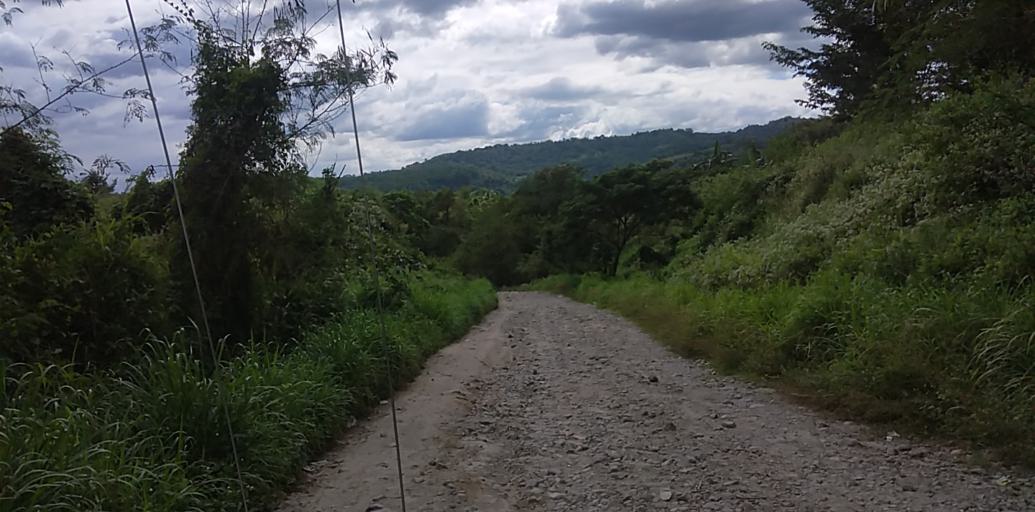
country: PH
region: Central Luzon
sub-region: Province of Pampanga
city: Dolores
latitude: 15.1149
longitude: 120.5049
